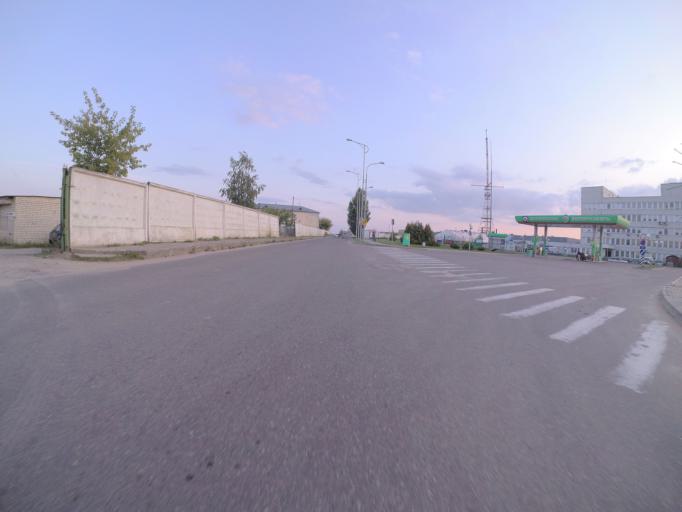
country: BY
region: Grodnenskaya
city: Hrodna
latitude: 53.7062
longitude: 23.8285
